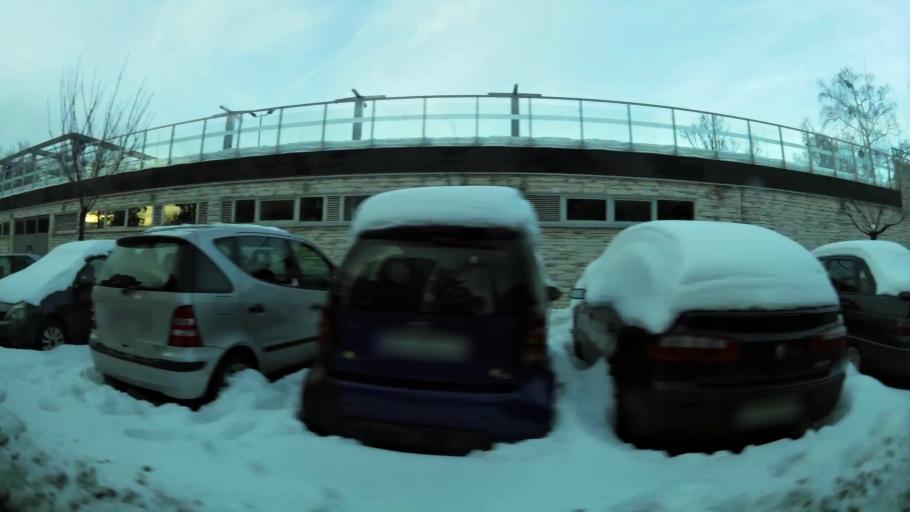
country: RS
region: Central Serbia
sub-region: Belgrade
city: Palilula
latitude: 44.7934
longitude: 20.5101
